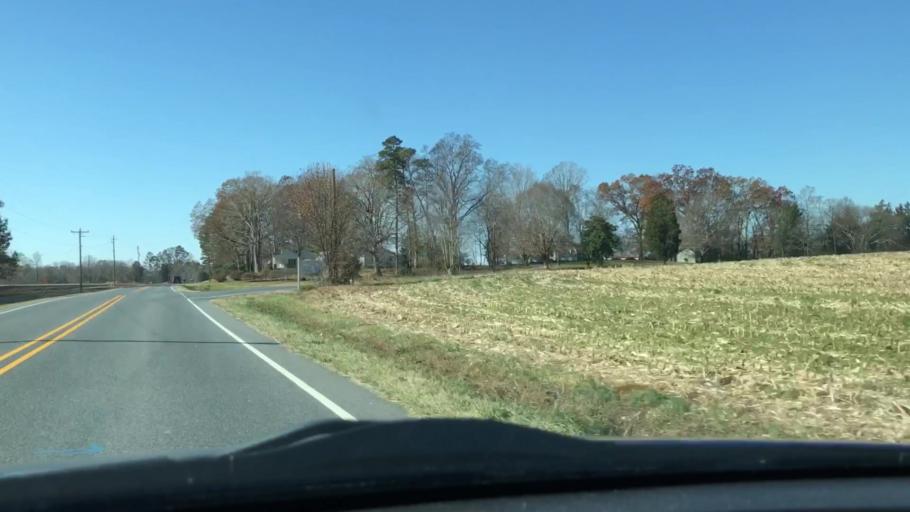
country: US
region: North Carolina
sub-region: Randolph County
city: Asheboro
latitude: 35.6732
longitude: -79.9268
